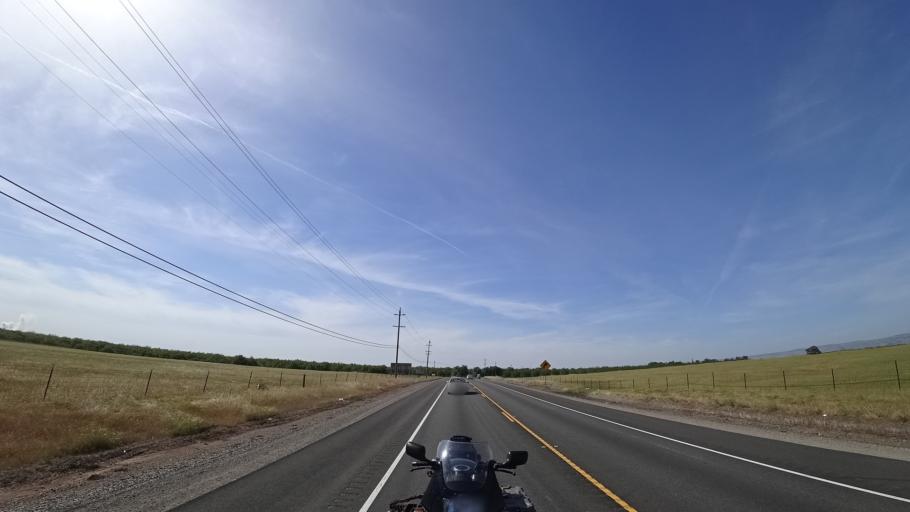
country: US
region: California
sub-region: Glenn County
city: Hamilton City
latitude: 39.8684
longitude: -121.9649
